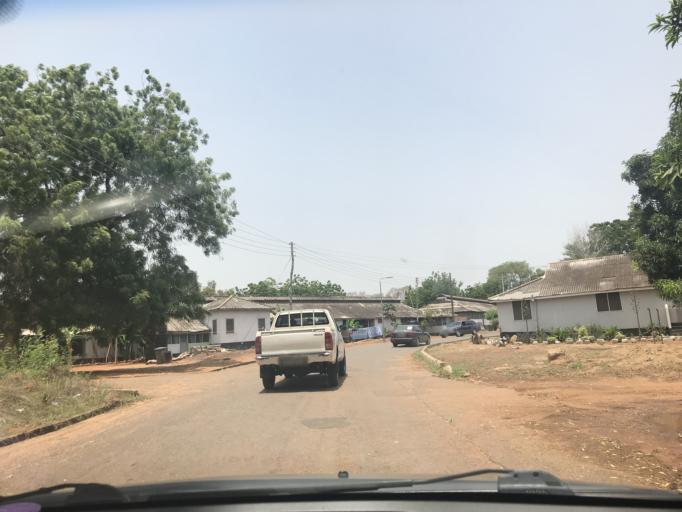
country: GH
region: Greater Accra
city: Teshi Old Town
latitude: 5.5848
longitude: -0.1540
